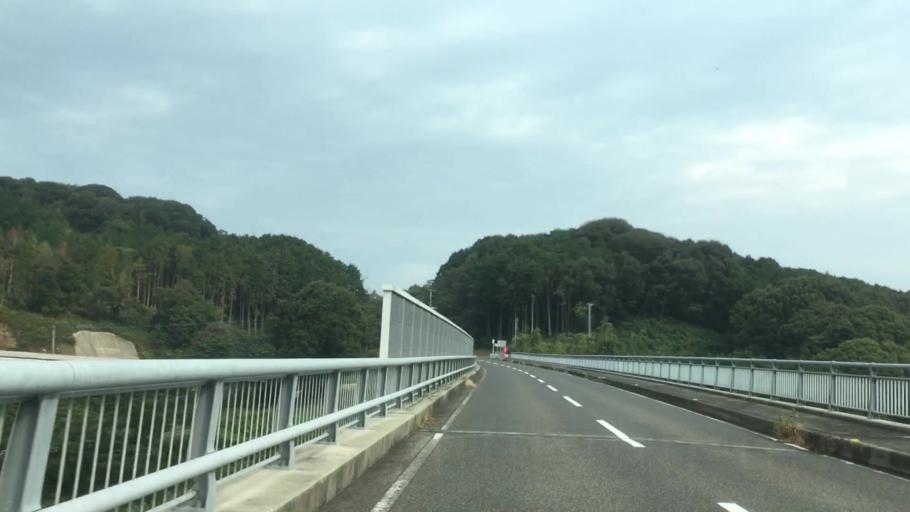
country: JP
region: Nagasaki
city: Sasebo
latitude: 33.0064
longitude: 129.7074
